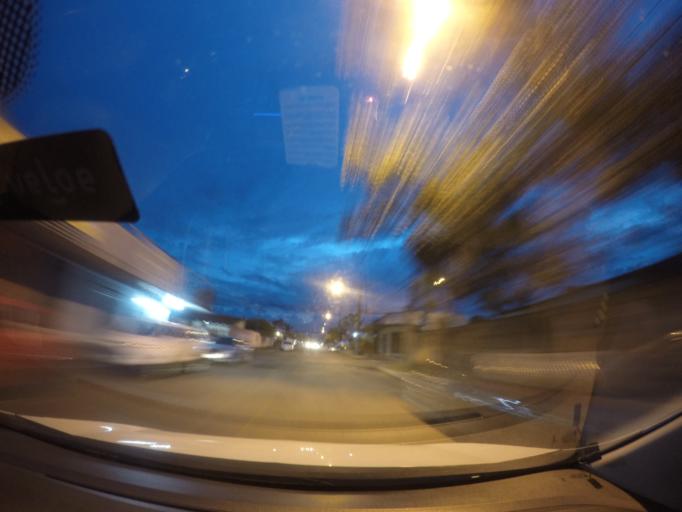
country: BR
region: Goias
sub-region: Goiania
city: Goiania
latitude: -16.7263
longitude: -49.3687
